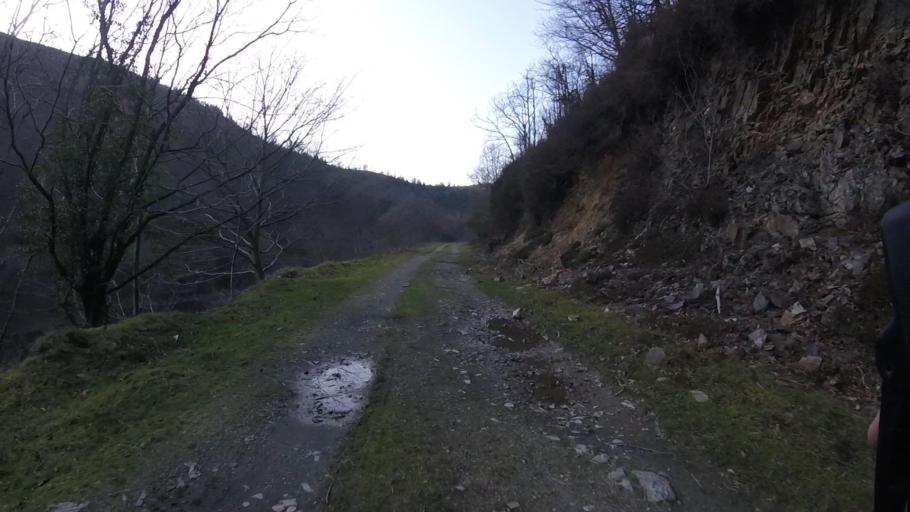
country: ES
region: Navarre
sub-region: Provincia de Navarra
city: Arano
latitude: 43.2175
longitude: -1.8646
